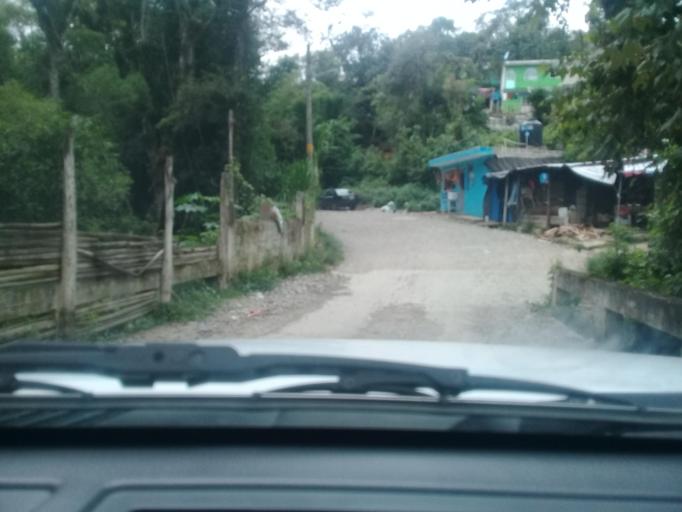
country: MX
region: Veracruz
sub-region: Tlalnelhuayocan
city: Otilpan
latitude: 19.5489
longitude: -96.9737
